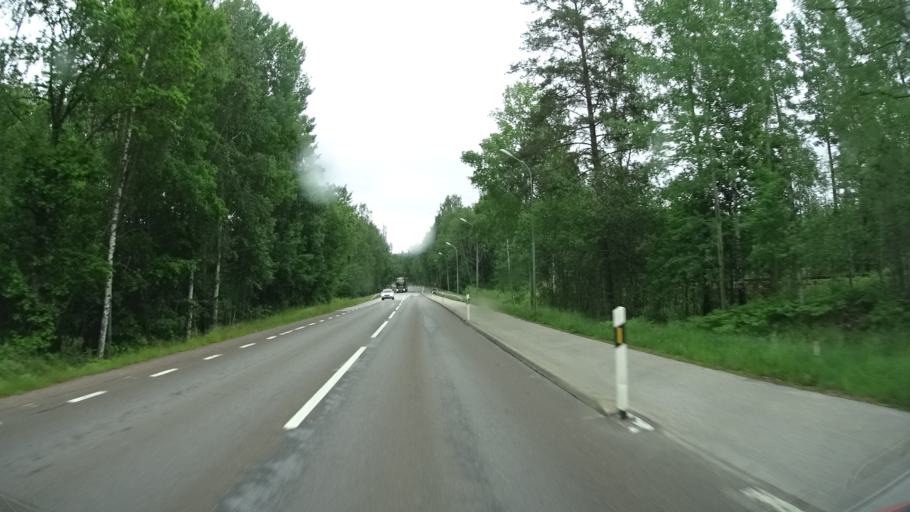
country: SE
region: Kalmar
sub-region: Hultsfreds Kommun
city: Hultsfred
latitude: 57.5471
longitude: 15.7306
